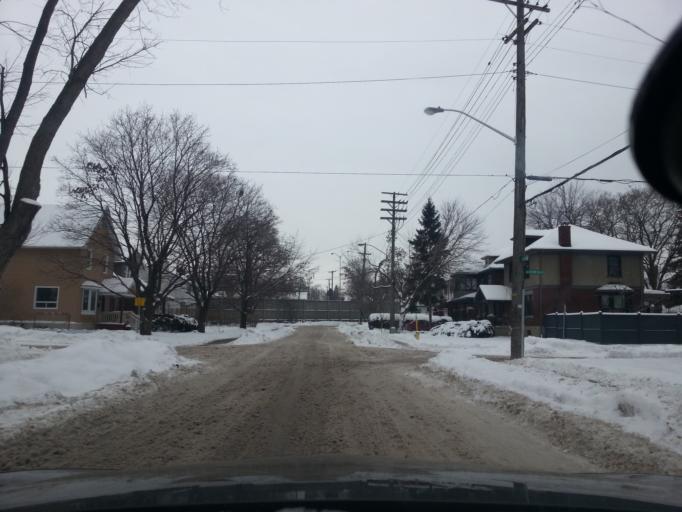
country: CA
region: Ontario
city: Ottawa
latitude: 45.3926
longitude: -75.7334
